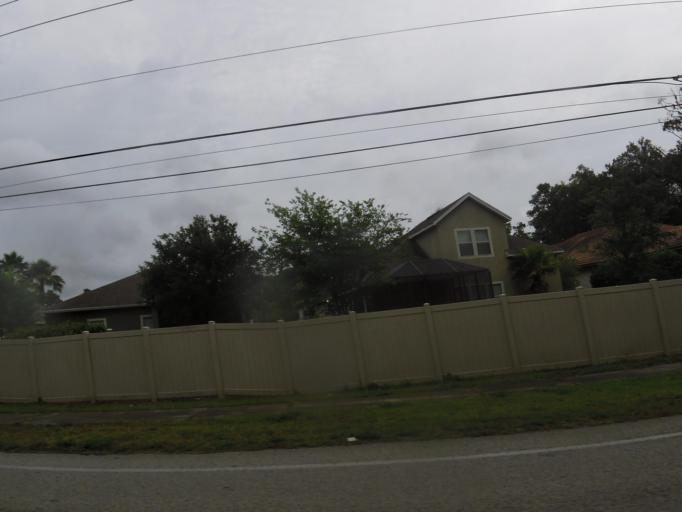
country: US
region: Florida
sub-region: Saint Johns County
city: Saint Augustine
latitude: 29.9111
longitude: -81.3647
